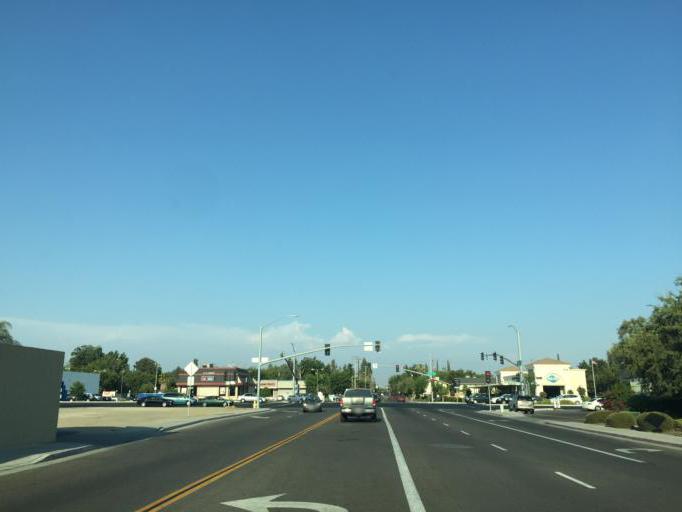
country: US
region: California
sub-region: Tulare County
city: Visalia
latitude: 36.3202
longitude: -119.3151
